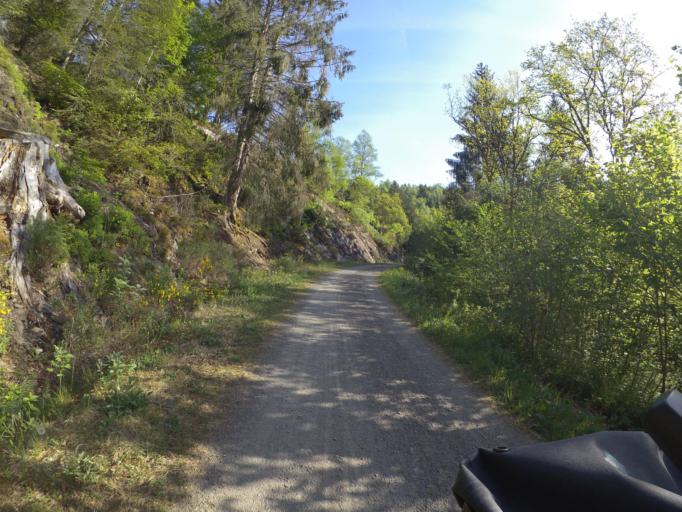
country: DE
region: North Rhine-Westphalia
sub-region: Regierungsbezirk Koln
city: Monschau
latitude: 50.5504
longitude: 6.2204
